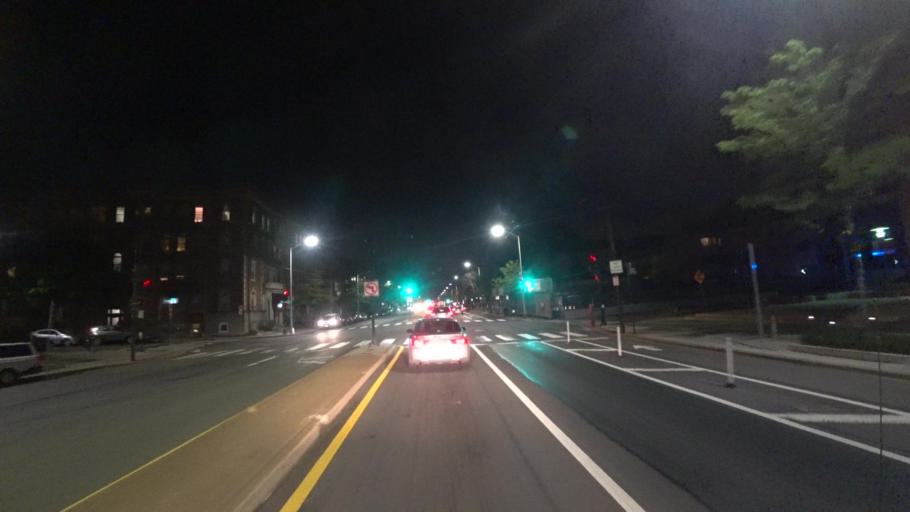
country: US
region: Massachusetts
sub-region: Middlesex County
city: Cambridge
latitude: 42.3798
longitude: -71.1200
